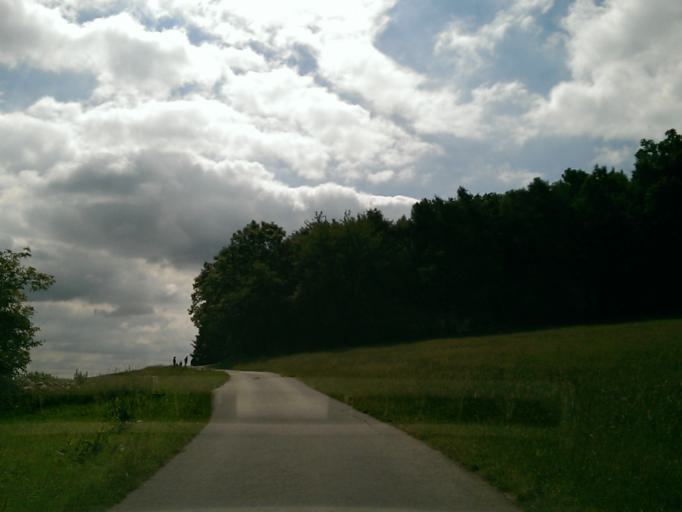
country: DE
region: Saxony
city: Eibau
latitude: 50.9632
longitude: 14.6892
